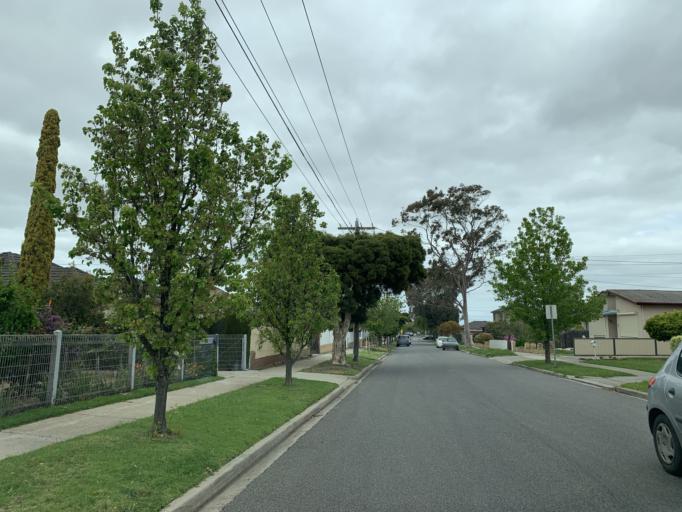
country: AU
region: Victoria
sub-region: Brimbank
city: St Albans
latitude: -37.7404
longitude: 144.8120
